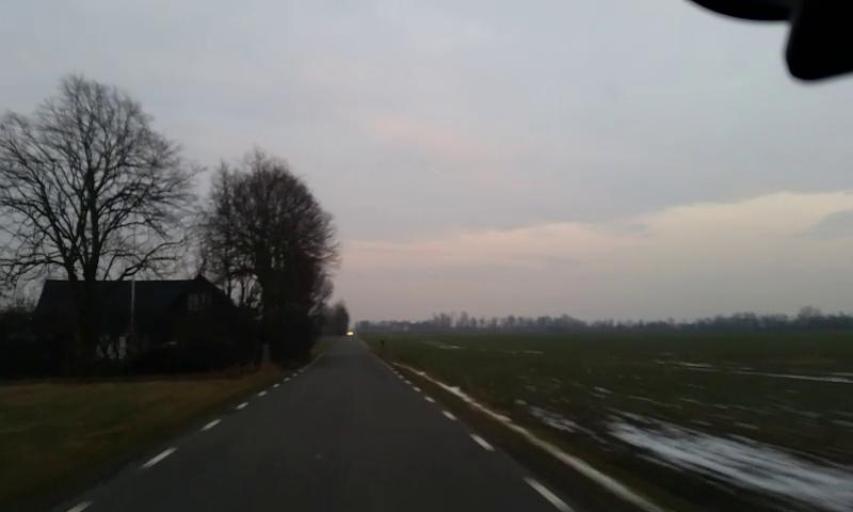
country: SE
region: Skane
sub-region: Angelholms Kommun
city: AEngelholm
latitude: 56.2788
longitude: 12.8662
